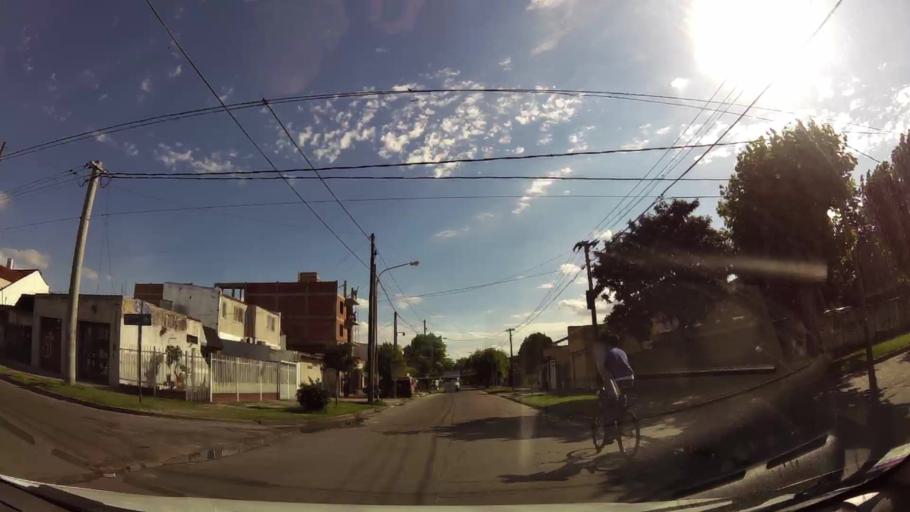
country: AR
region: Buenos Aires
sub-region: Partido de Moron
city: Moron
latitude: -34.6582
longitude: -58.5895
